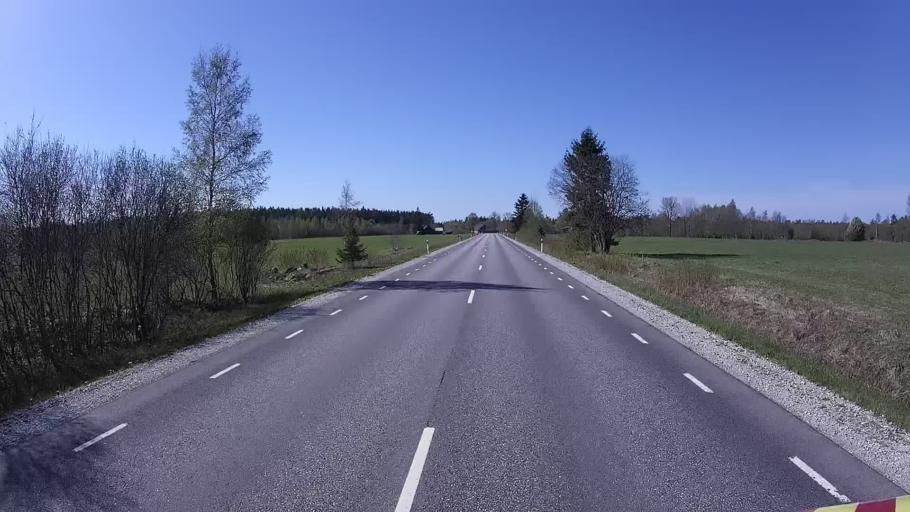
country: EE
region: Raplamaa
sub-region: Jaervakandi vald
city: Jarvakandi
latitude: 58.7376
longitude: 24.8059
